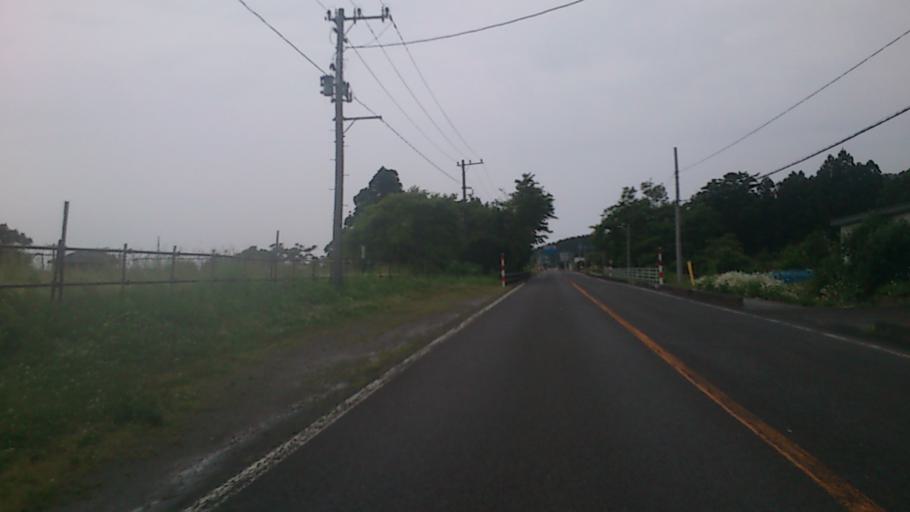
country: JP
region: Akita
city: Noshiromachi
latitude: 40.4057
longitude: 139.9682
